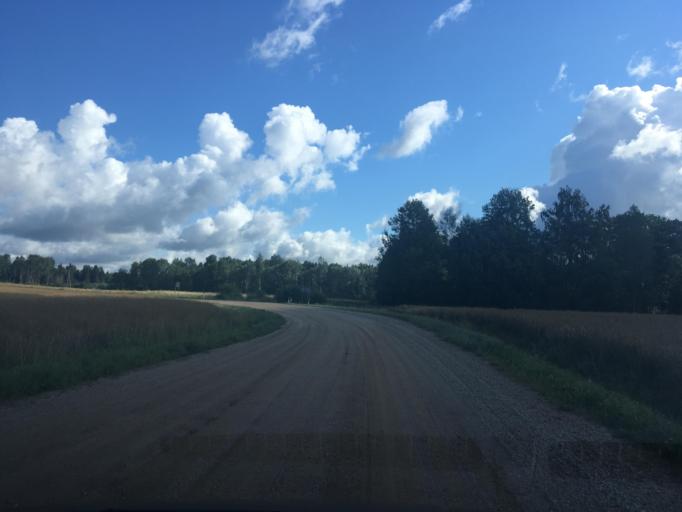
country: EE
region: Jogevamaa
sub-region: Poltsamaa linn
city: Poltsamaa
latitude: 58.4792
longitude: 25.9684
